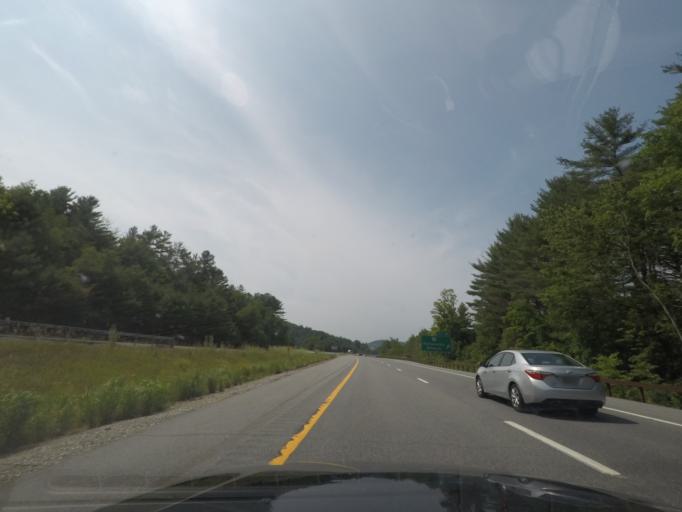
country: US
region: New York
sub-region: Warren County
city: Warrensburg
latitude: 43.7208
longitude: -73.8169
